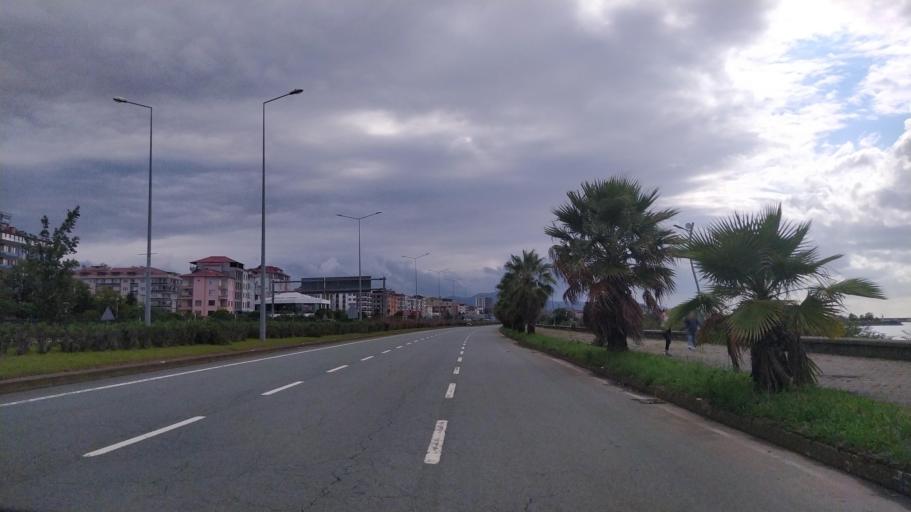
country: TR
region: Rize
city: Ardesen
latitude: 41.1963
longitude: 40.9998
